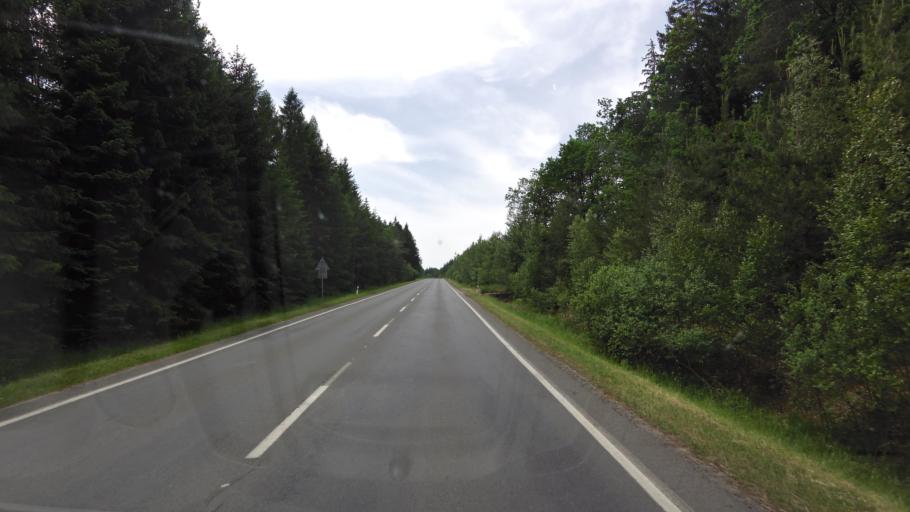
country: CZ
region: Plzensky
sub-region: Okres Rokycany
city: Rokycany
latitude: 49.7192
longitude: 13.5686
